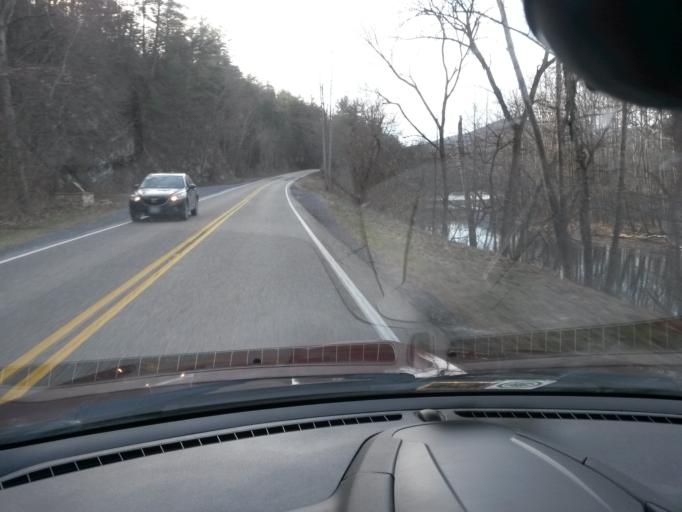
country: US
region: Virginia
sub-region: Alleghany County
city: Clifton Forge
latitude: 37.8970
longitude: -79.7424
